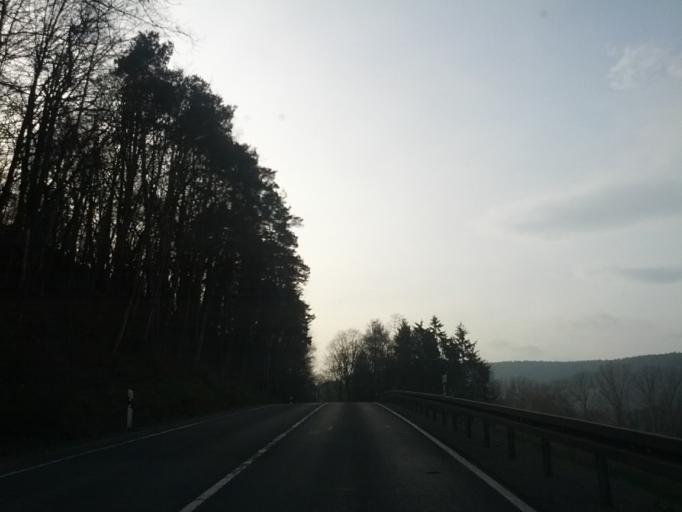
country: DE
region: Thuringia
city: Schwallungen
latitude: 50.6790
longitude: 10.3533
